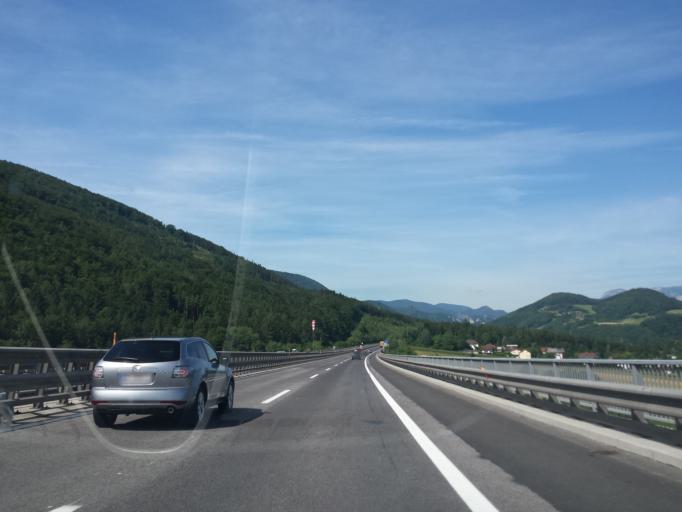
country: AT
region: Lower Austria
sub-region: Politischer Bezirk Neunkirchen
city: Enzenreith
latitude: 47.6633
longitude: 15.9555
